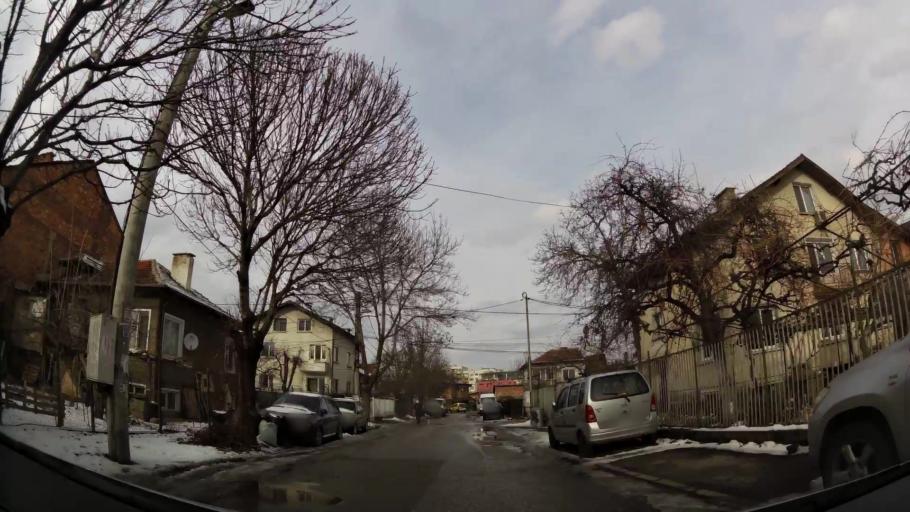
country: BG
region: Sofia-Capital
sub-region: Stolichna Obshtina
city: Sofia
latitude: 42.7057
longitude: 23.3822
